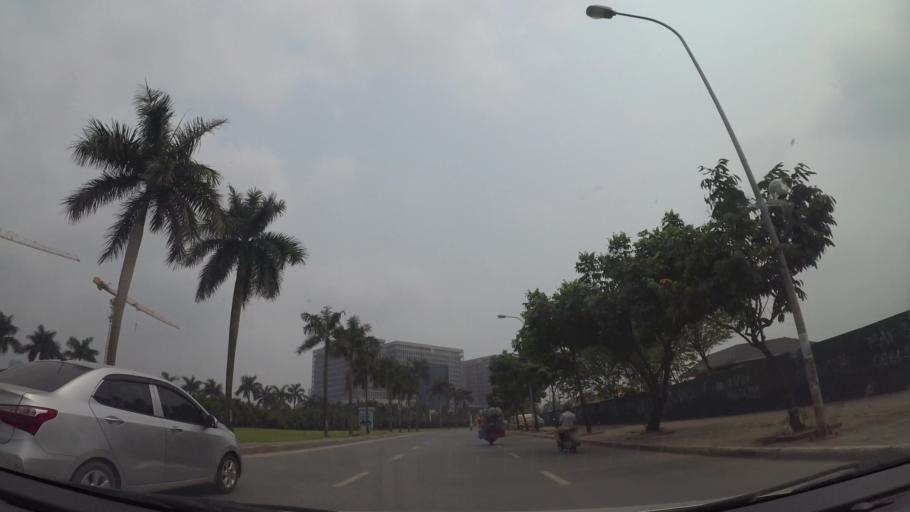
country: VN
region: Ha Noi
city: Thanh Xuan
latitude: 21.0092
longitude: 105.7729
